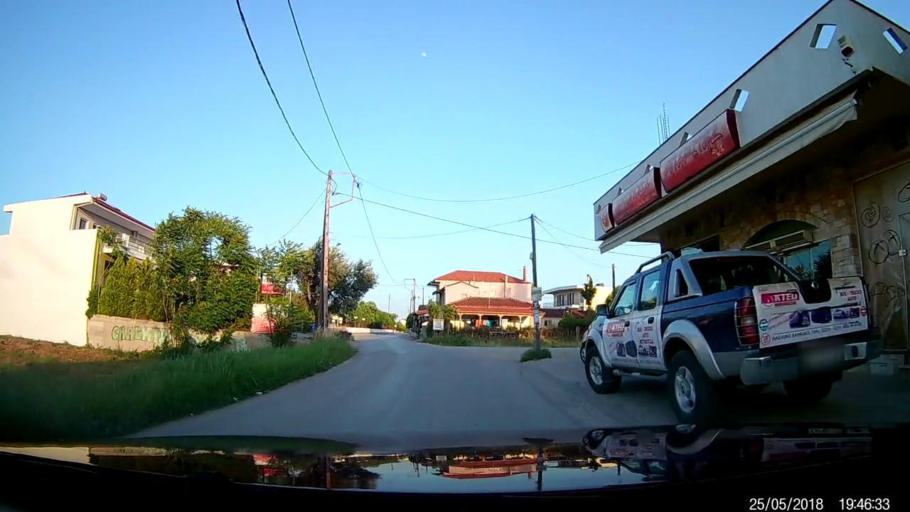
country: GR
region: Central Greece
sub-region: Nomos Evvoias
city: Ayios Nikolaos
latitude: 38.4261
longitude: 23.6404
